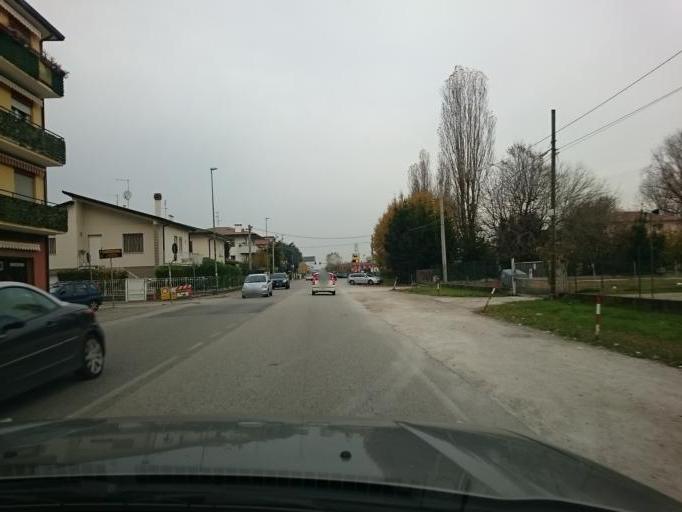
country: IT
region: Veneto
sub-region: Provincia di Padova
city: Caselle
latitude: 45.4115
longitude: 11.8256
